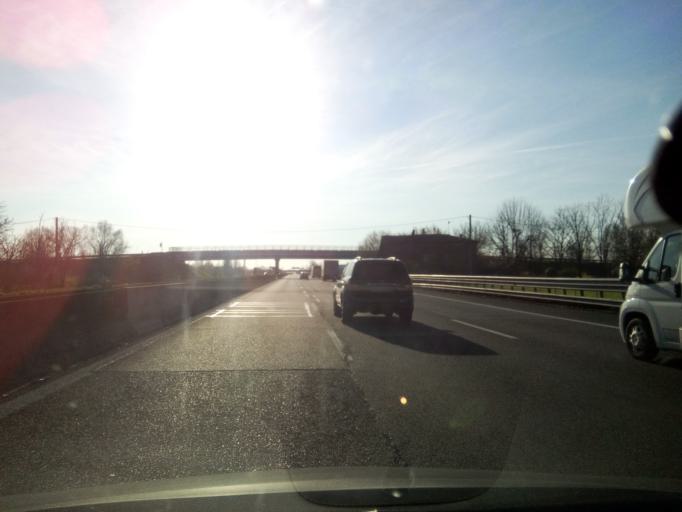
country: IT
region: Emilia-Romagna
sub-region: Provincia di Parma
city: Baganzola
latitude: 44.8441
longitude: 10.3212
